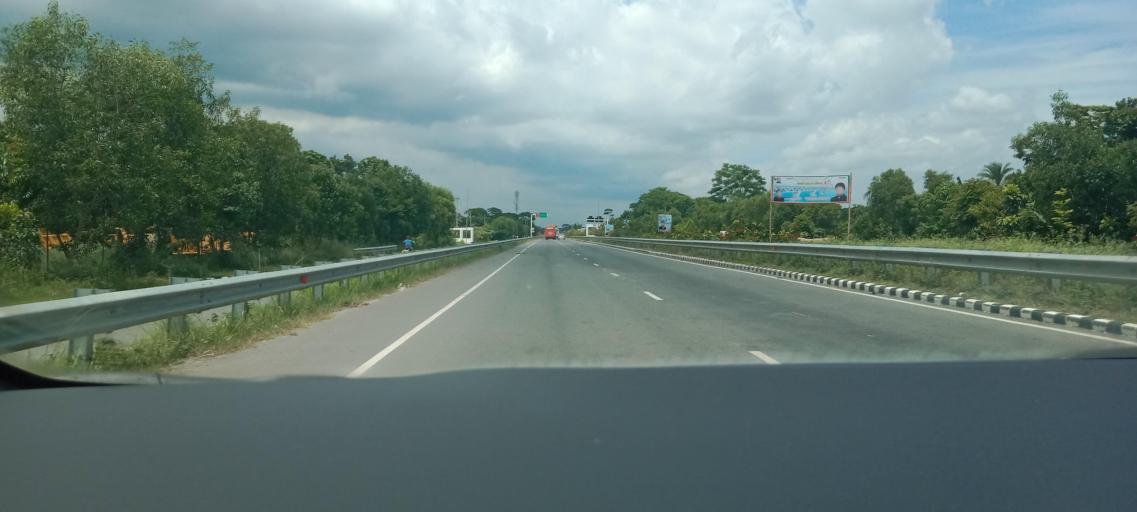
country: BD
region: Dhaka
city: Char Bhadrasan
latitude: 23.3712
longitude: 90.0849
